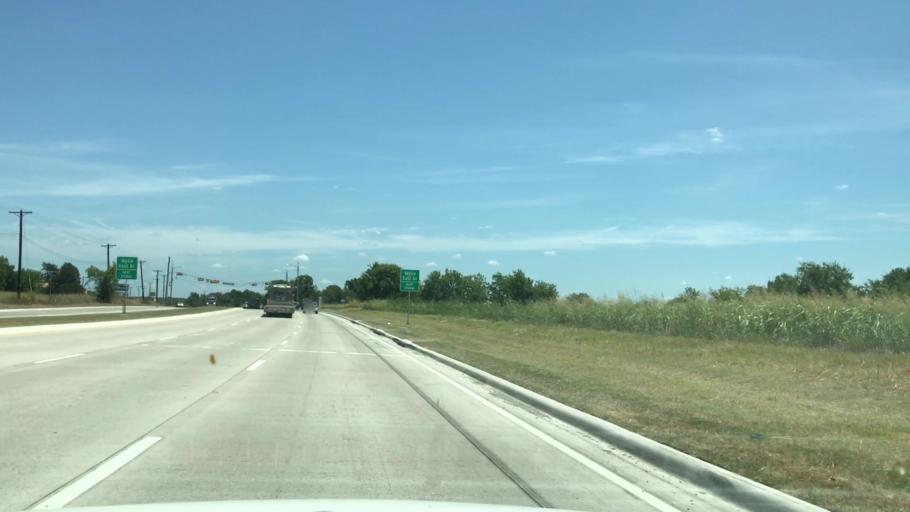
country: US
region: Texas
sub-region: Collin County
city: Wylie
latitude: 33.0226
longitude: -96.4985
